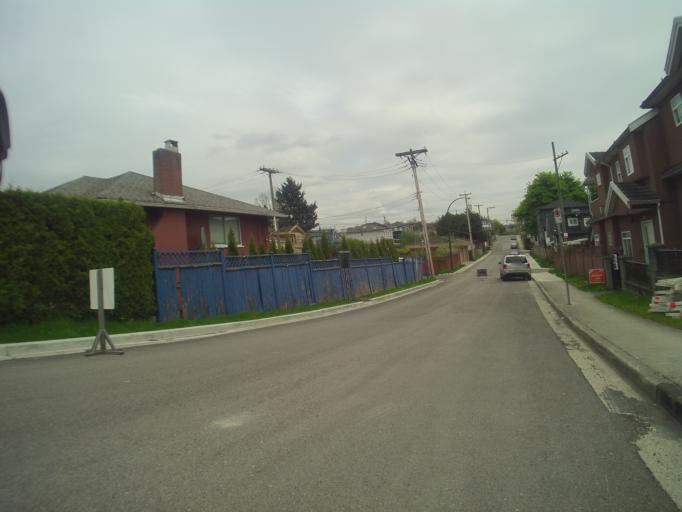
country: CA
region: British Columbia
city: Vancouver
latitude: 49.2430
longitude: -123.0762
